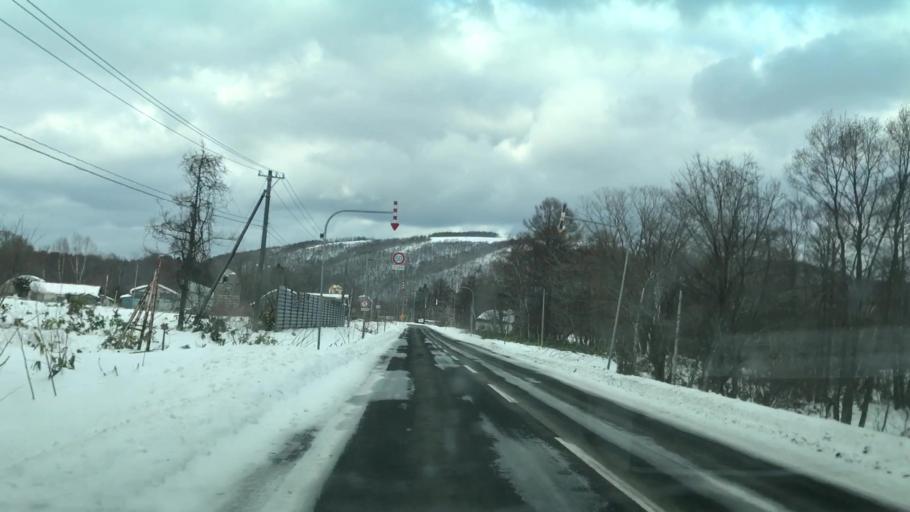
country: JP
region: Hokkaido
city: Yoichi
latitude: 43.3140
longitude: 140.5432
